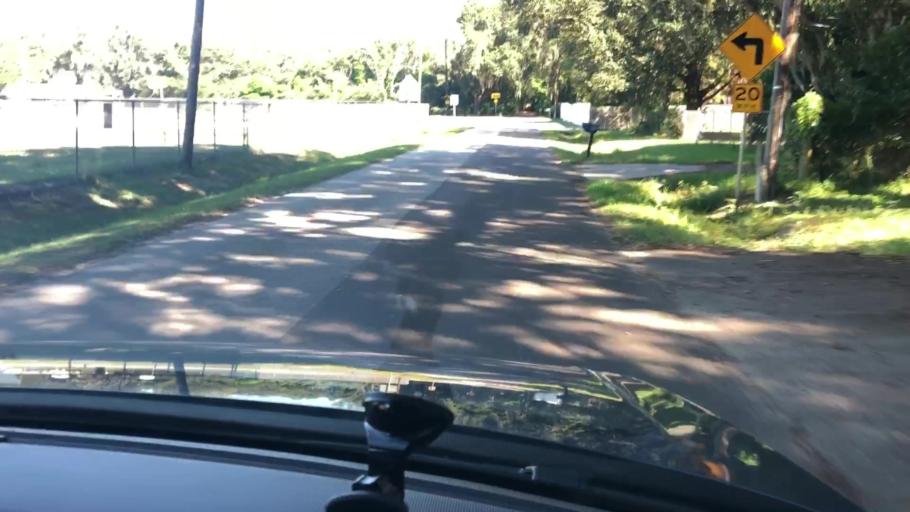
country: US
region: Florida
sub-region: Polk County
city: Kathleen
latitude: 28.1244
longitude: -82.0182
